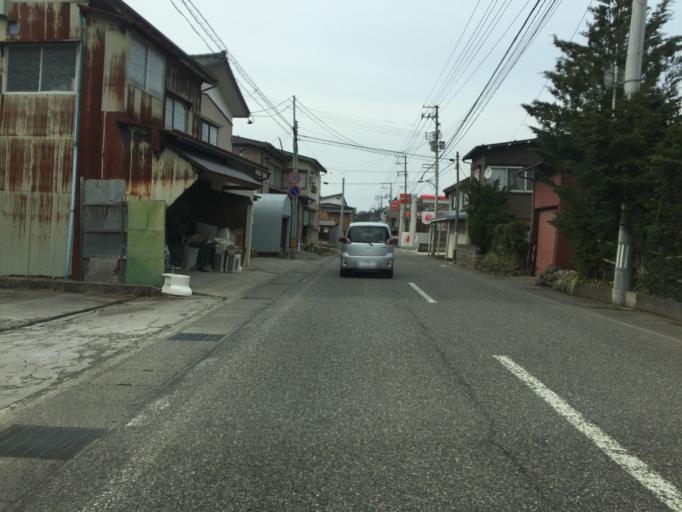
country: JP
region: Niigata
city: Tochio-honcho
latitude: 37.4673
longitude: 139.0037
